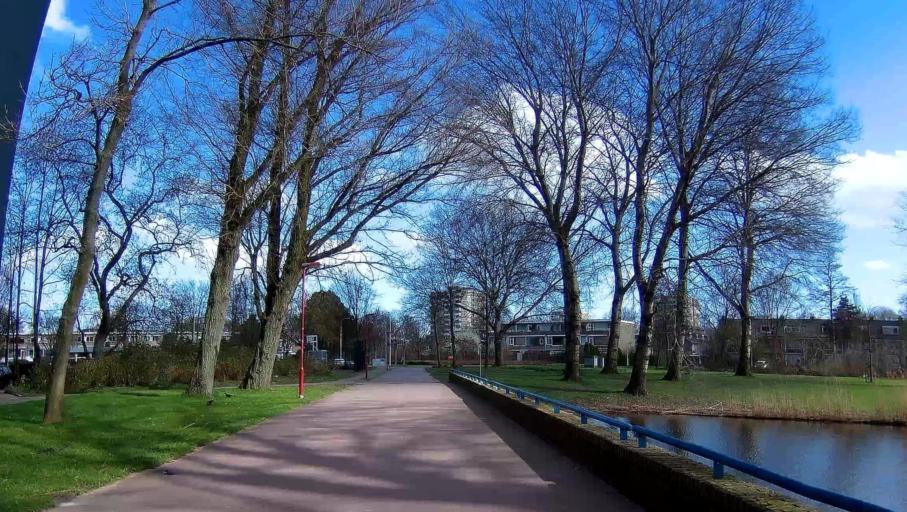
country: NL
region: South Holland
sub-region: Gemeente Zoetermeer
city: Zoetermeer
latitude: 52.0498
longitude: 4.4807
